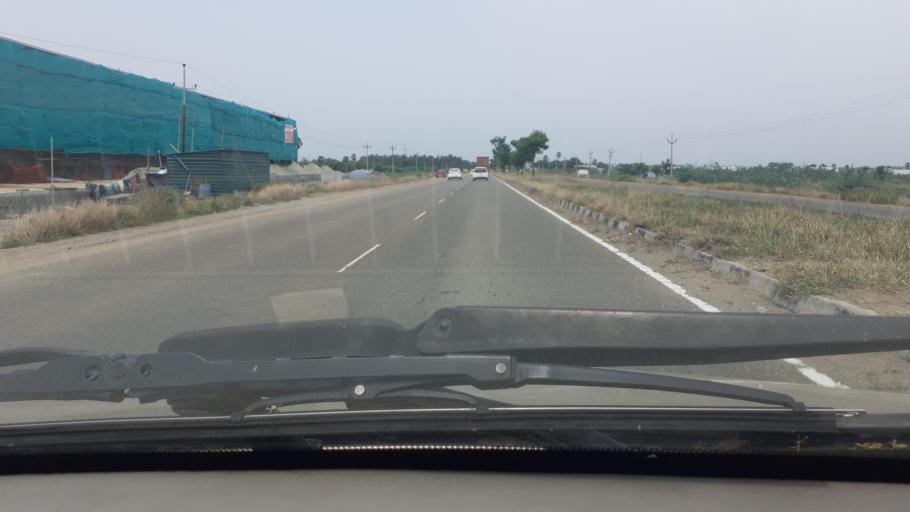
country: IN
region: Tamil Nadu
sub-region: Thoothukkudi
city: Eral
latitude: 8.7346
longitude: 77.9789
